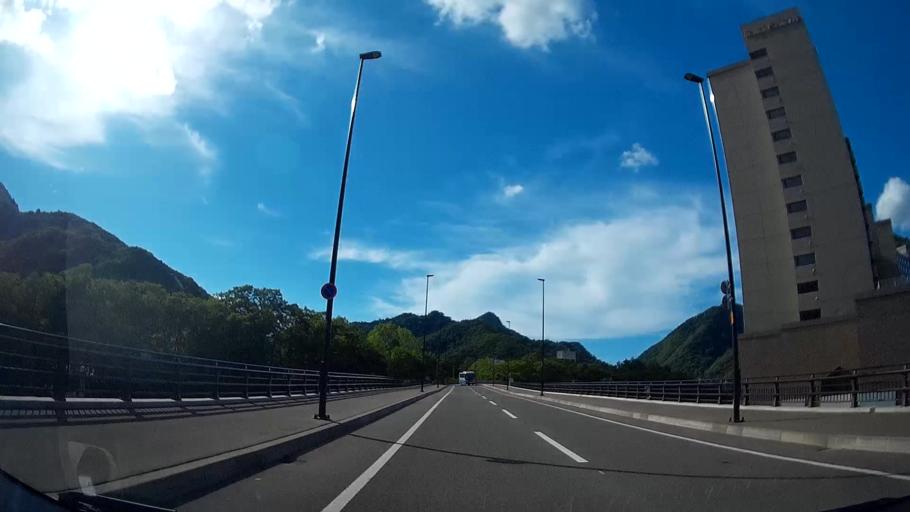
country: JP
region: Hokkaido
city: Sapporo
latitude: 42.9682
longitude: 141.1671
